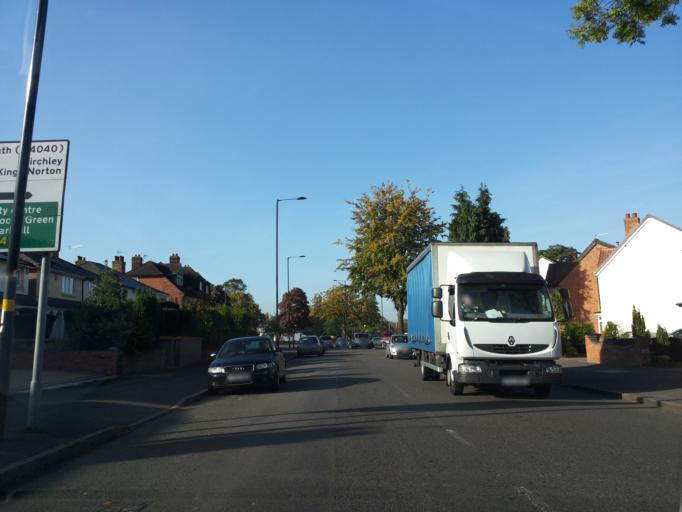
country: GB
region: England
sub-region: Solihull
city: Shirley
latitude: 52.4234
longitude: -1.8343
